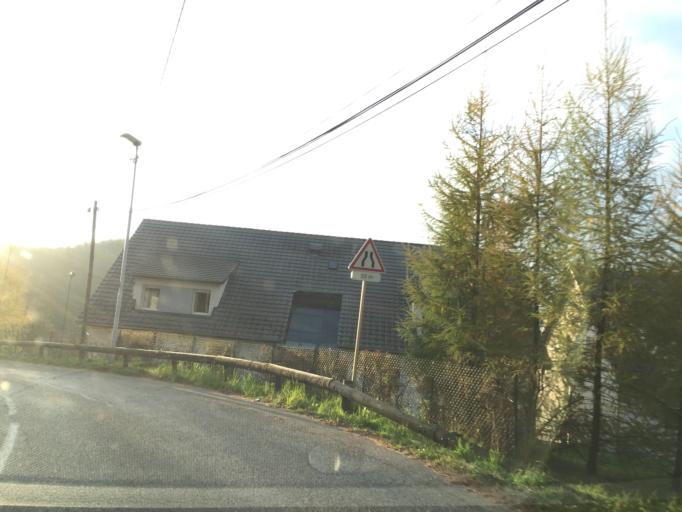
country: FR
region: Rhone-Alpes
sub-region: Departement de la Savoie
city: Sonnaz
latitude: 45.5988
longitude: 5.9073
